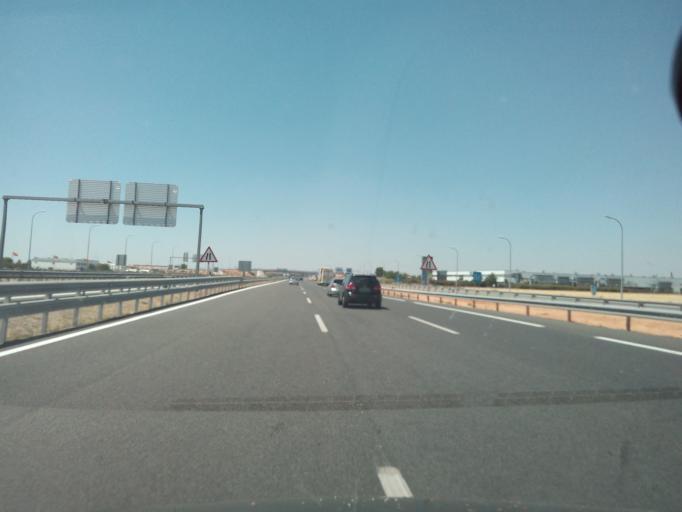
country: ES
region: Castille-La Mancha
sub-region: Province of Toledo
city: Ocana
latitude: 39.9302
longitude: -3.4848
